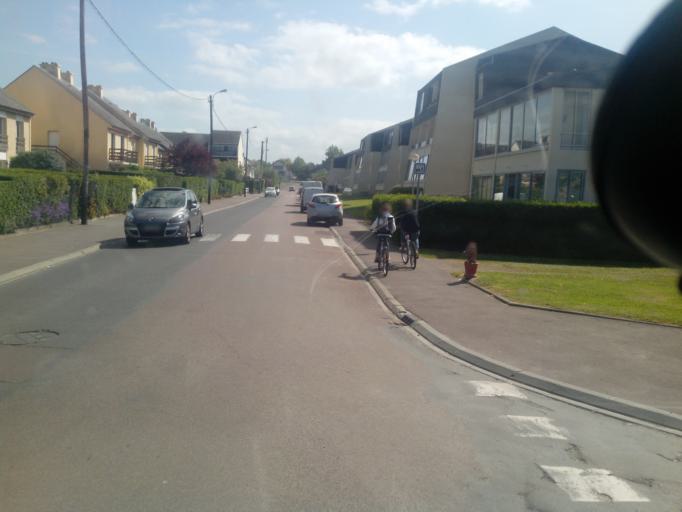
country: FR
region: Lower Normandy
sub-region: Departement du Calvados
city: Courseulles-sur-Mer
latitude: 49.3331
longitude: -0.4460
